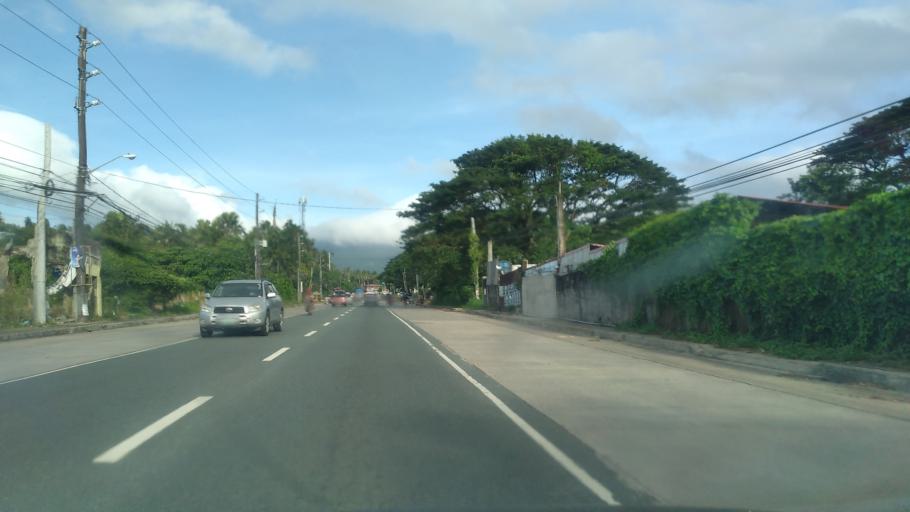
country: PH
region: Calabarzon
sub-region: Province of Quezon
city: Isabang
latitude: 13.9729
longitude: 121.5596
